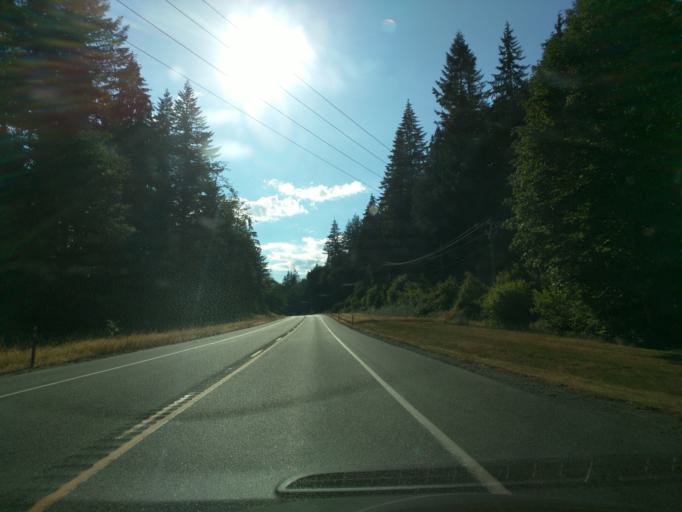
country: US
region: Washington
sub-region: Snohomish County
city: Darrington
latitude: 48.2779
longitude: -121.7564
